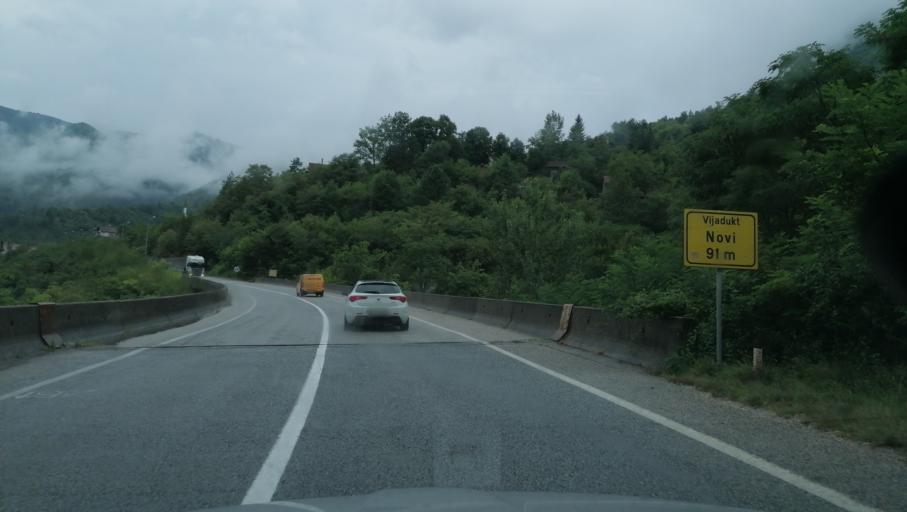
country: BA
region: Republika Srpska
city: Visegrad
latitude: 43.7333
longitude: 19.1833
